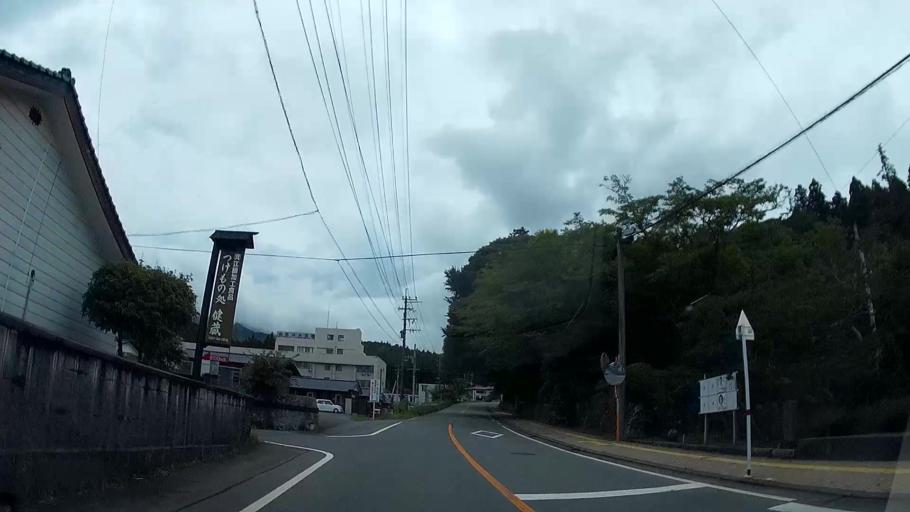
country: JP
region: Kumamoto
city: Aso
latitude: 32.9317
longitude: 131.0798
